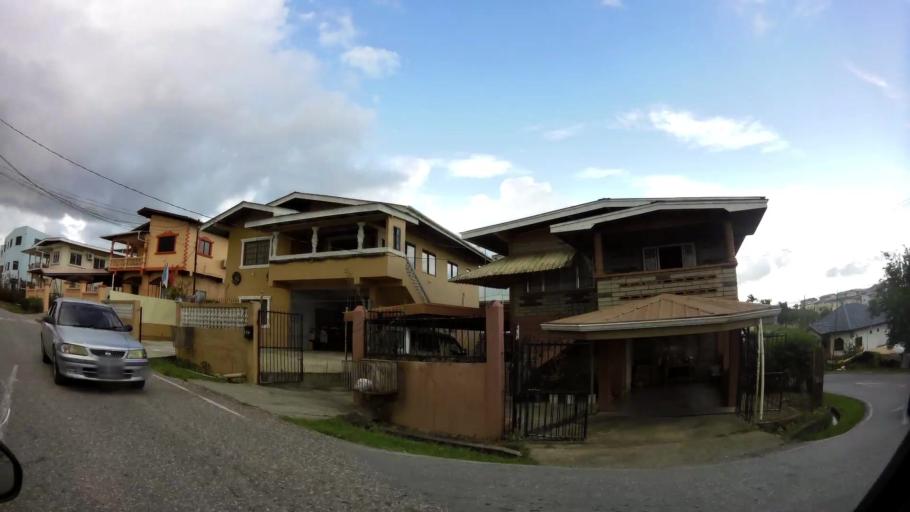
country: TT
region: Penal/Debe
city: Debe
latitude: 10.2421
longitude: -61.4415
